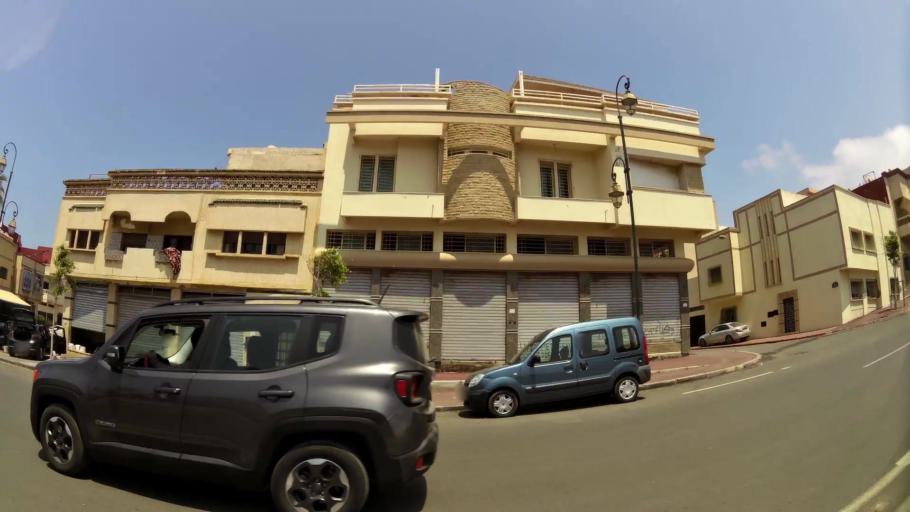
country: MA
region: Rabat-Sale-Zemmour-Zaer
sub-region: Skhirate-Temara
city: Temara
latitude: 33.9736
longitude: -6.8978
